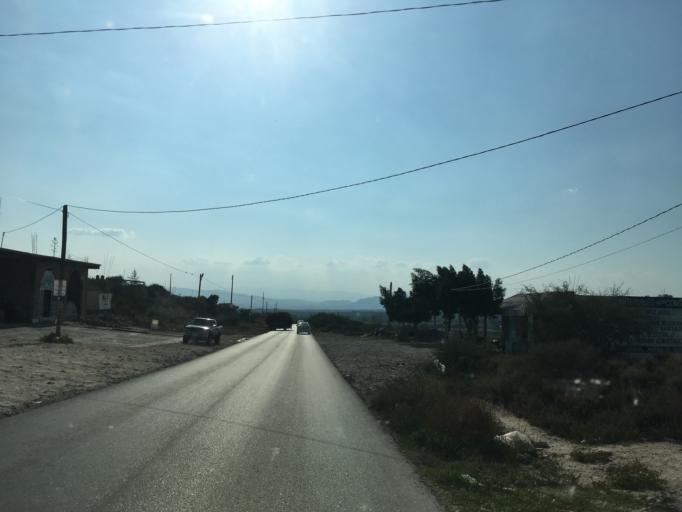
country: MX
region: Hidalgo
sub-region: Ixmiquilpan
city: El Nith
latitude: 20.5629
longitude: -99.1510
